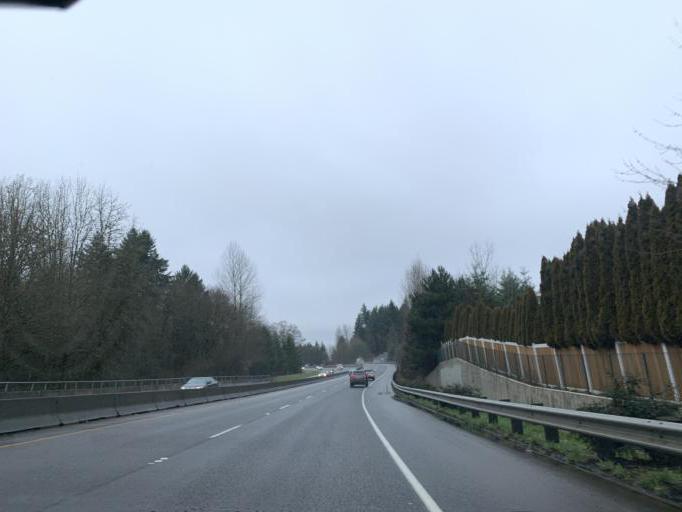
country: US
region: Washington
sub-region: Clark County
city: Five Corners
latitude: 45.6831
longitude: -122.5844
